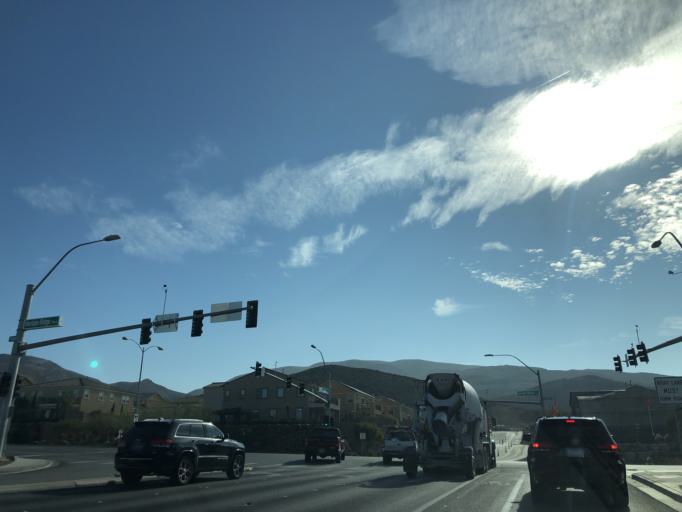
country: US
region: Nevada
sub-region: Clark County
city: Henderson
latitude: 36.0224
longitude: -115.0297
